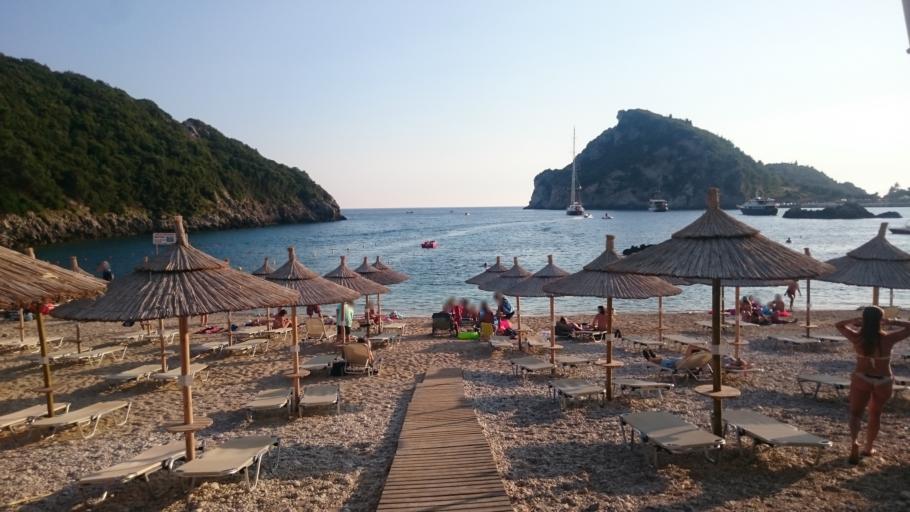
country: GR
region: Ionian Islands
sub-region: Nomos Kerkyras
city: Agios Georgis
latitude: 39.6735
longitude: 19.7155
